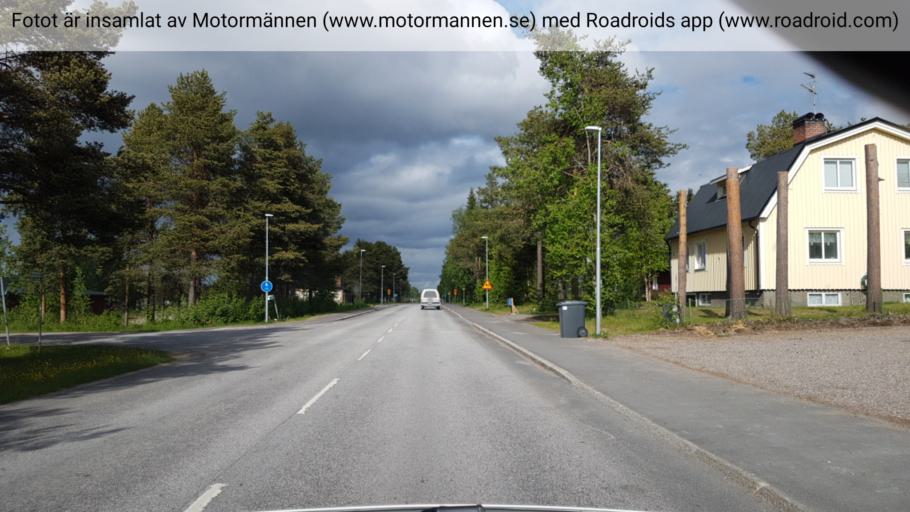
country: SE
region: Norrbotten
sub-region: Gallivare Kommun
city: Malmberget
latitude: 67.6758
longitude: 21.6323
